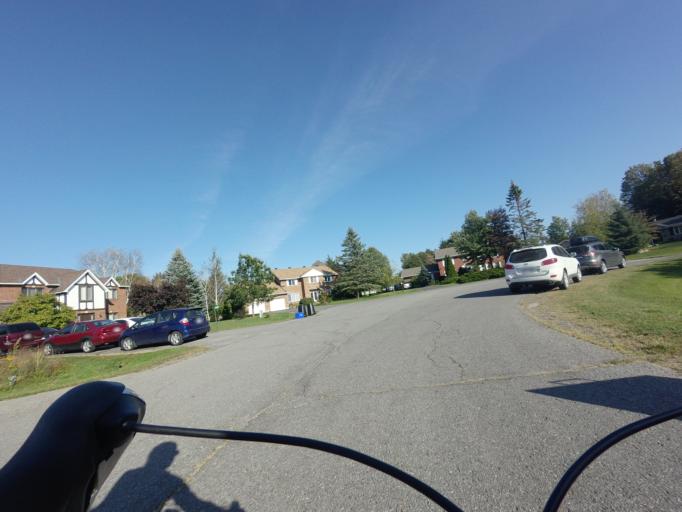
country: CA
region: Ontario
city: Bells Corners
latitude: 45.2288
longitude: -75.6756
